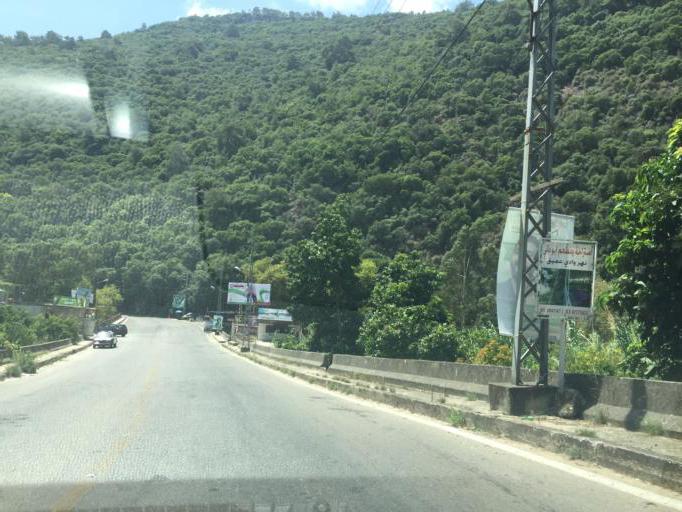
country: LB
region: Mont-Liban
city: Beit ed Dine
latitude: 33.7021
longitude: 35.4683
